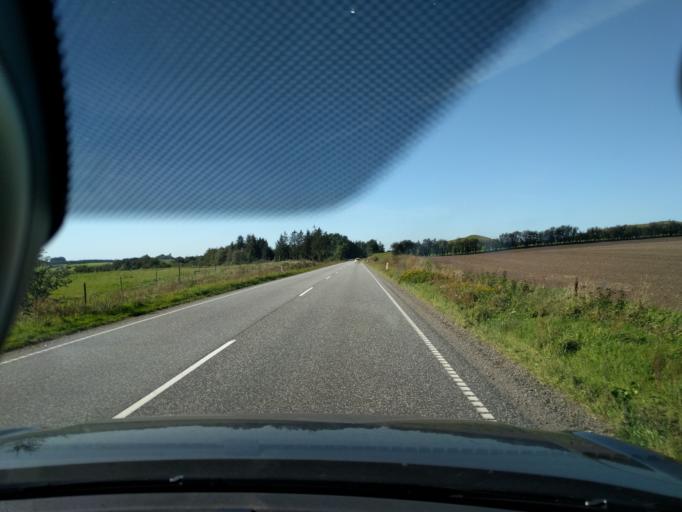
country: DK
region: North Denmark
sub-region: Mariagerfjord Kommune
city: Hobro
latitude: 56.6694
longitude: 9.7107
